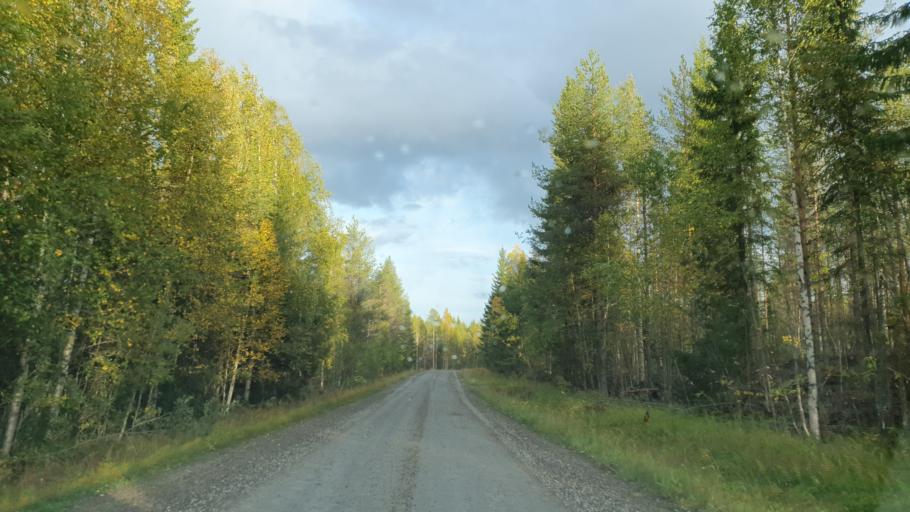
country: FI
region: Kainuu
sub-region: Kehys-Kainuu
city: Kuhmo
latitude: 64.4223
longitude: 29.3585
